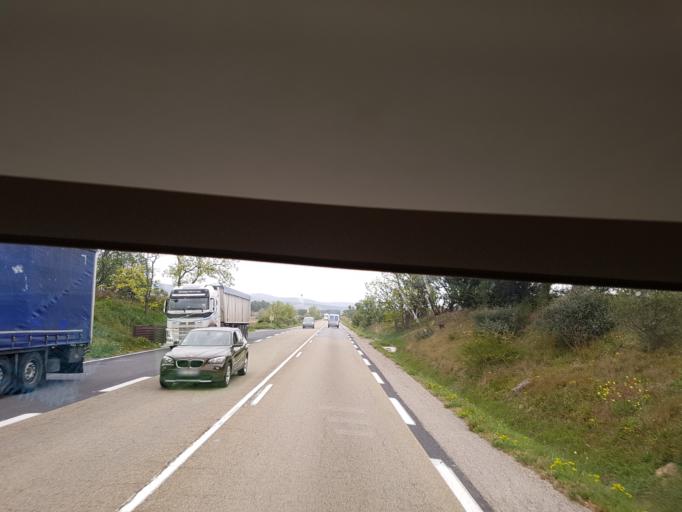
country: FR
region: Languedoc-Roussillon
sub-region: Departement de l'Aude
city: Peyriac-de-Mer
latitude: 43.0786
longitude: 2.9430
